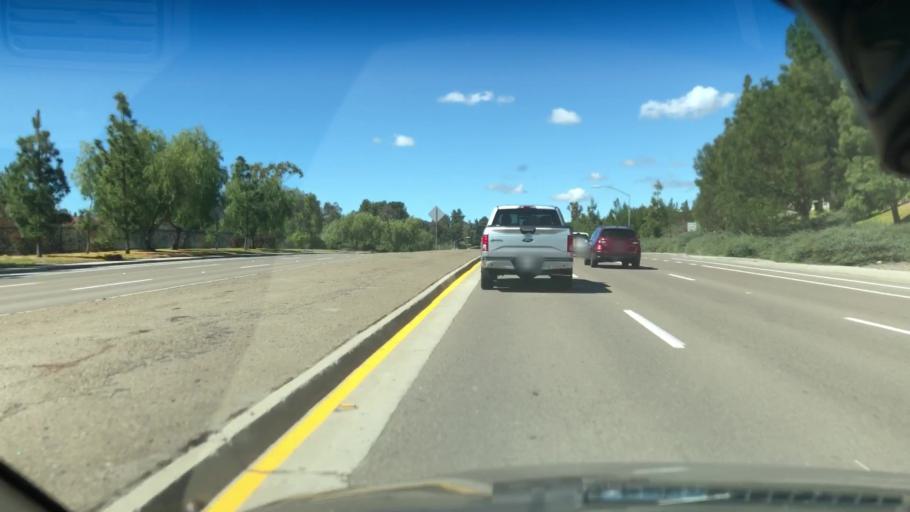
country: US
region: California
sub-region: San Diego County
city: Poway
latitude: 32.9891
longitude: -117.0692
